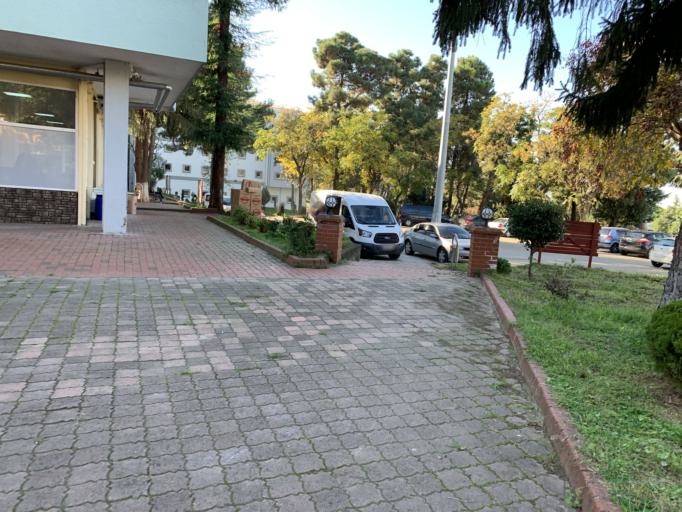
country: TR
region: Trabzon
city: Trabzon
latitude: 40.9958
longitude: 39.7690
